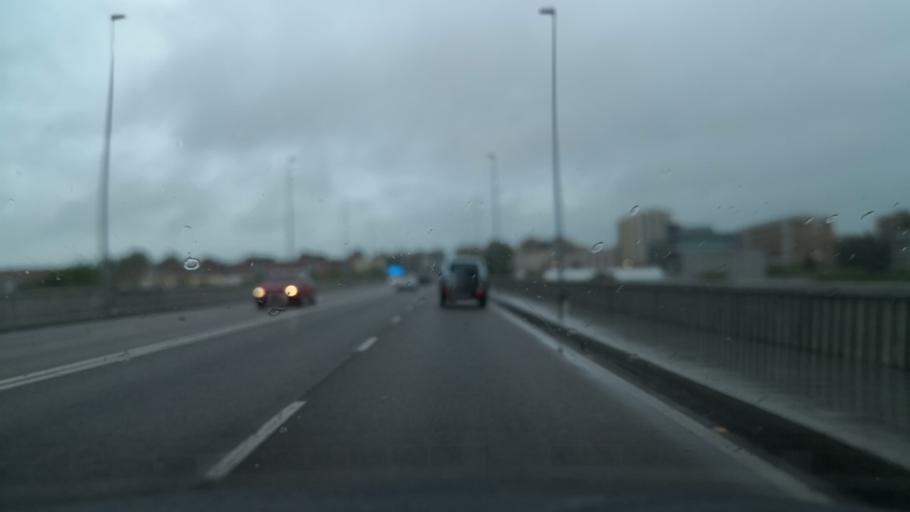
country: ES
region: Extremadura
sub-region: Provincia de Badajoz
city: Badajoz
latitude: 38.8808
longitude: -6.9827
